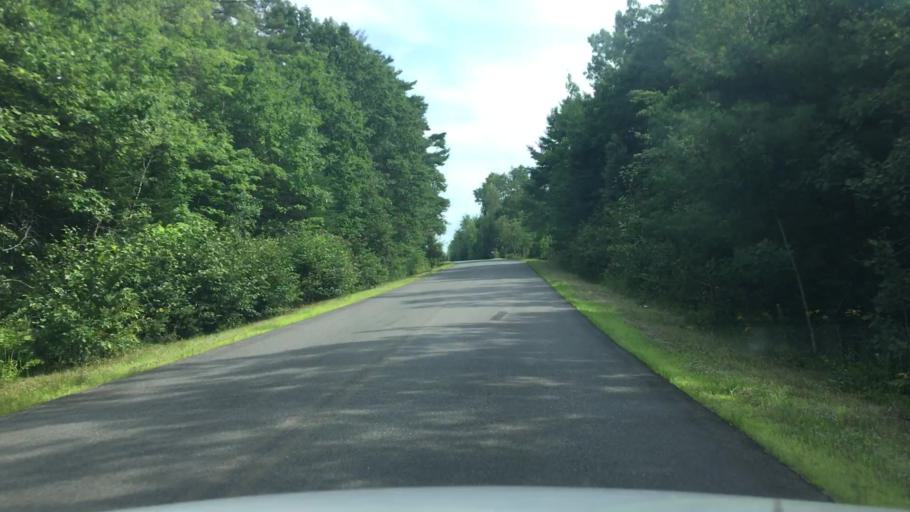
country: US
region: Maine
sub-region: Lincoln County
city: Jefferson
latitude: 44.2436
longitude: -69.4460
